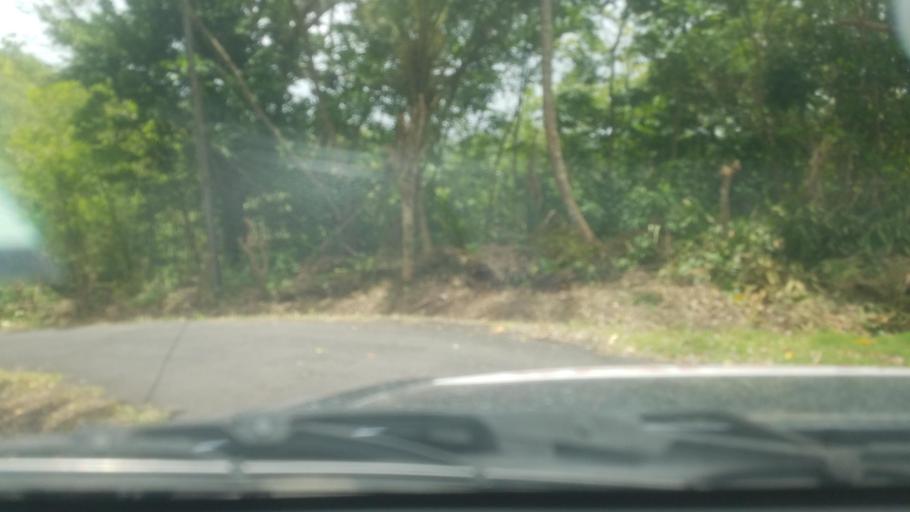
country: LC
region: Laborie Quarter
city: Laborie
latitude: 13.7664
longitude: -60.9867
